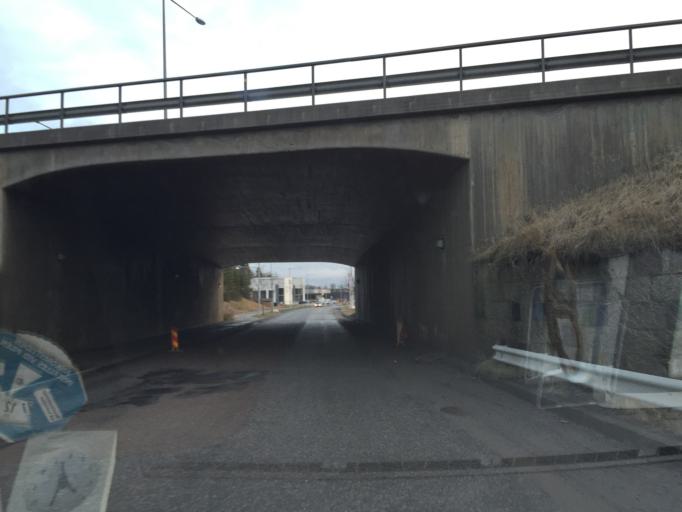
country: SE
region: Stockholm
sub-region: Sodertalje Kommun
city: Soedertaelje
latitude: 59.2019
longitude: 17.6686
